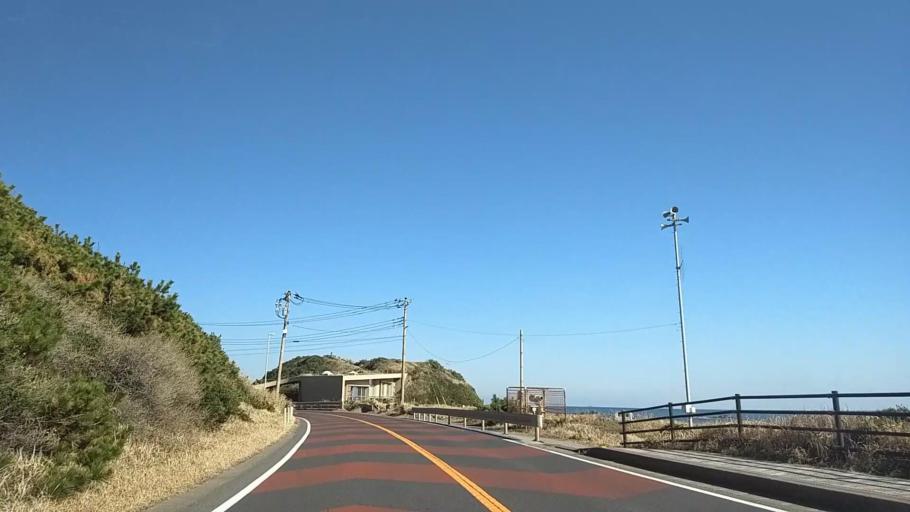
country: JP
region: Chiba
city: Hasaki
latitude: 35.7183
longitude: 140.8692
